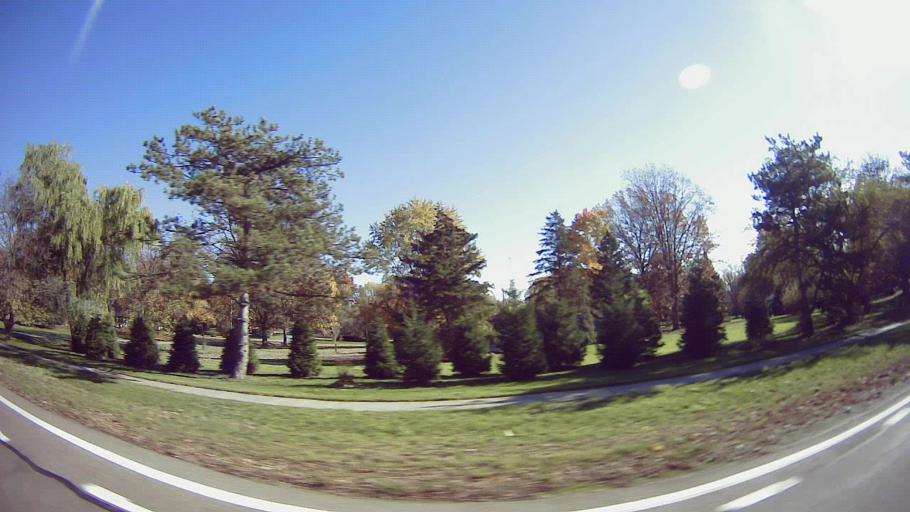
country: US
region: Michigan
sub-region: Oakland County
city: Farmington Hills
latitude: 42.4781
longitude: -83.3771
